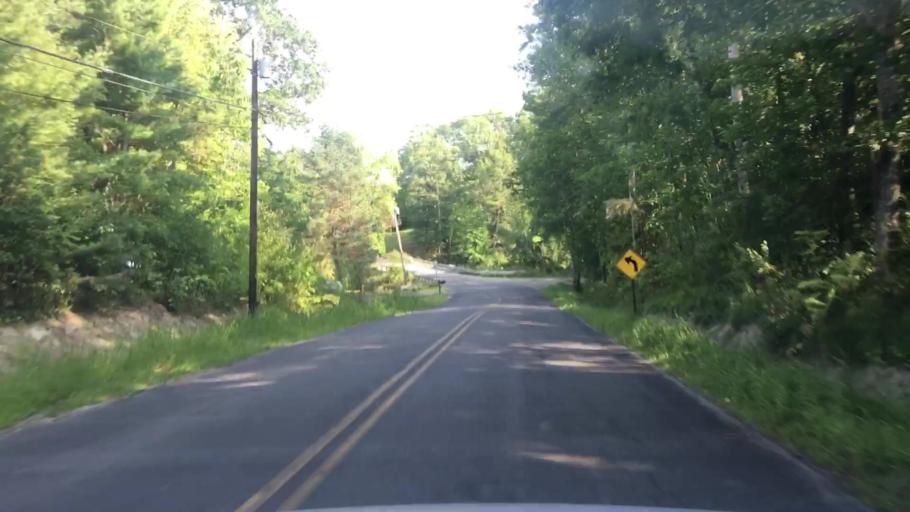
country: US
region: Maine
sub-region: Kennebec County
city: Waterville
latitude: 44.5810
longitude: -69.6713
